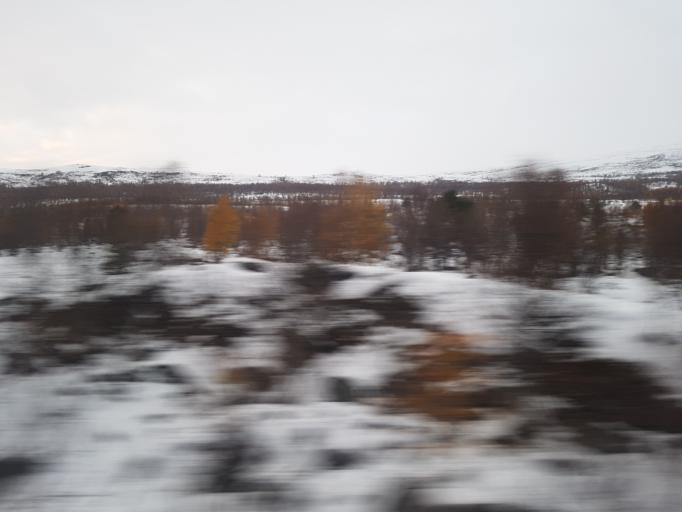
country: NO
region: Oppland
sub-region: Dovre
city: Dovre
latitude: 62.1666
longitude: 9.3858
